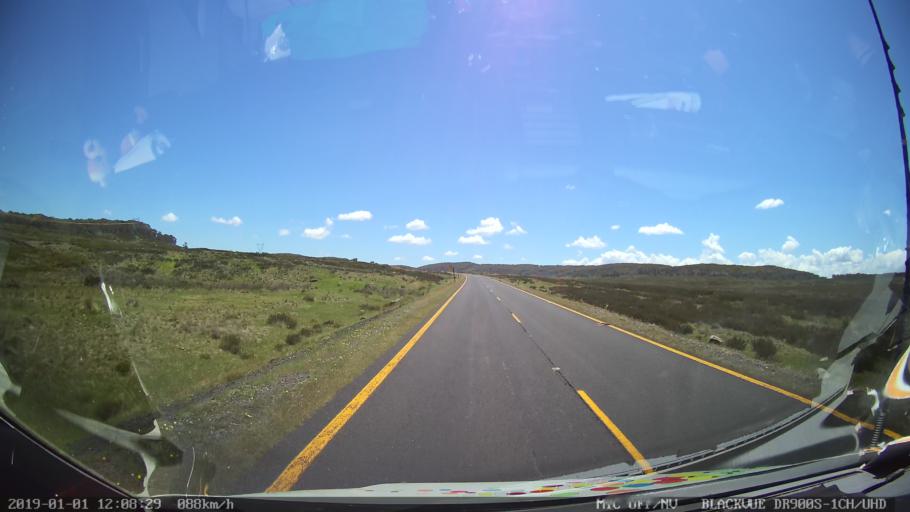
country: AU
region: New South Wales
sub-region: Tumut Shire
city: Tumut
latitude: -35.8196
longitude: 148.4951
